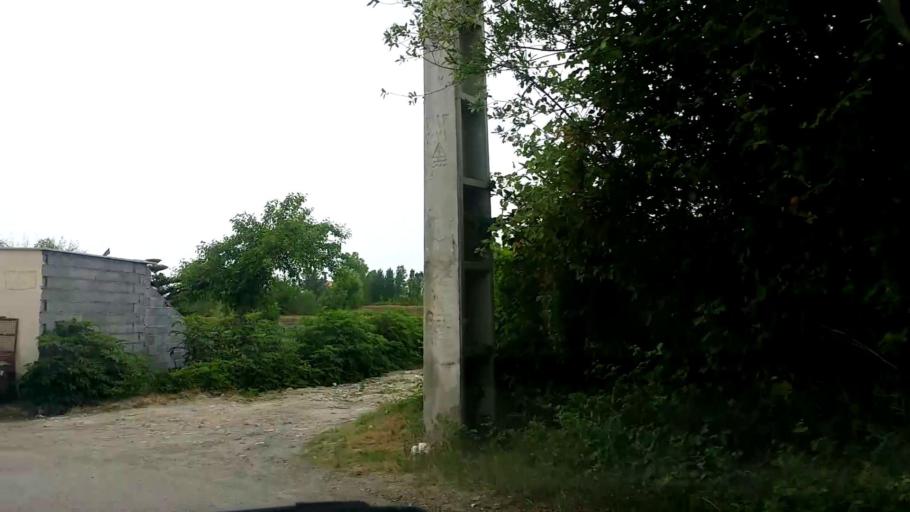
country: IR
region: Mazandaran
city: Chalus
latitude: 36.6543
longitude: 51.4071
